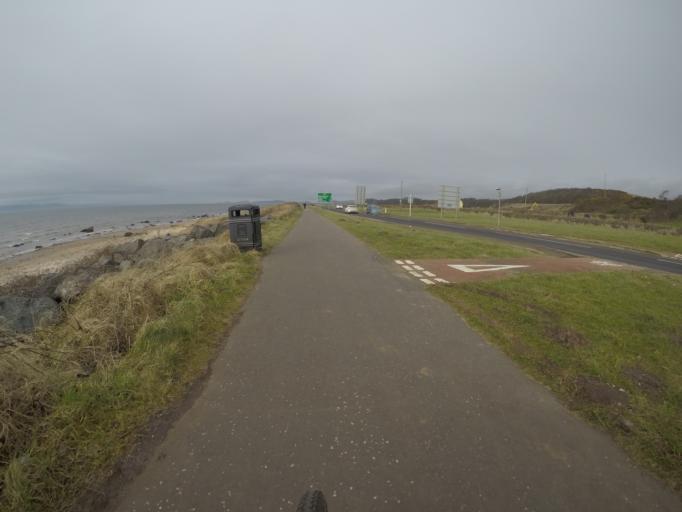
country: GB
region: Scotland
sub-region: North Ayrshire
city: Ardrossan
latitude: 55.6555
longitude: -4.8262
